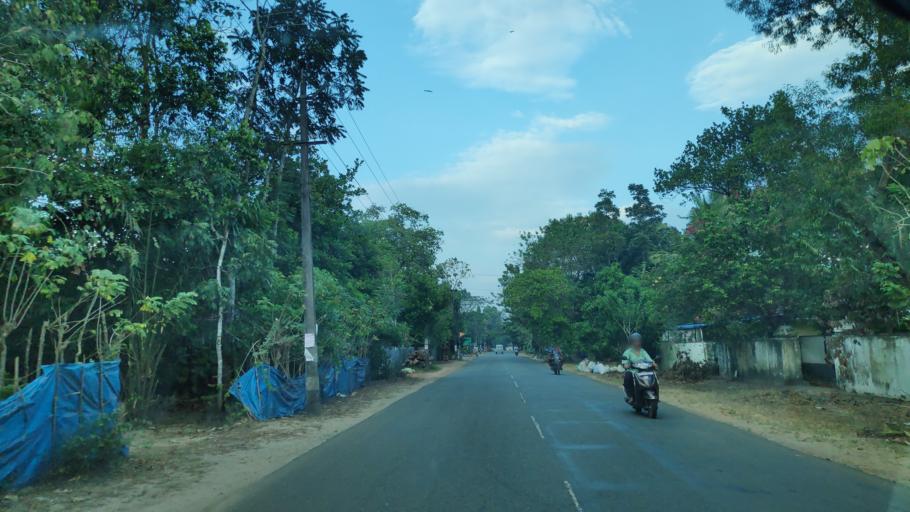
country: IN
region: Kerala
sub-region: Alappuzha
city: Shertallai
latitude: 9.6491
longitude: 76.3721
